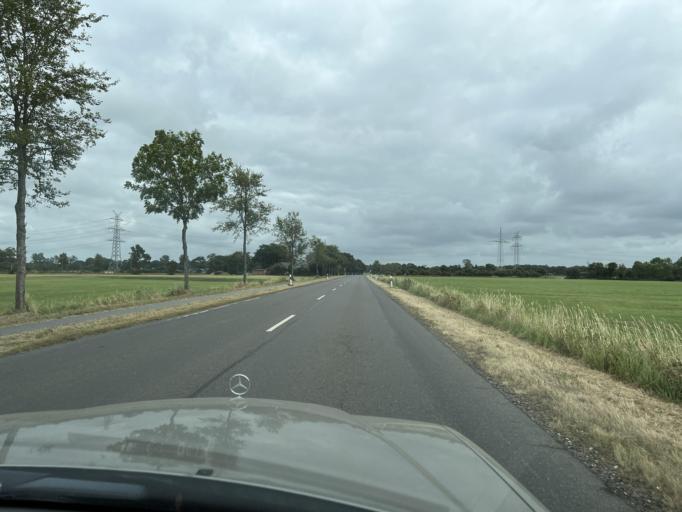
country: DE
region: Schleswig-Holstein
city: Stelle-Wittenwurth
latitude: 54.2468
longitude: 9.0723
